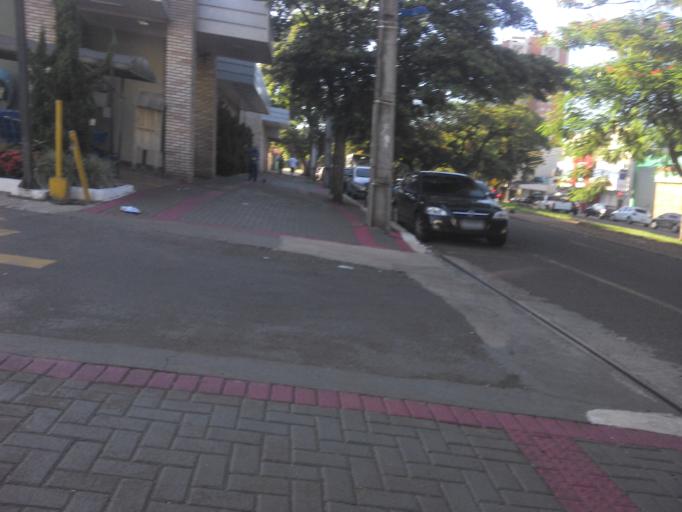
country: BR
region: Parana
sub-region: Maringa
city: Maringa
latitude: -23.4355
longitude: -51.9340
